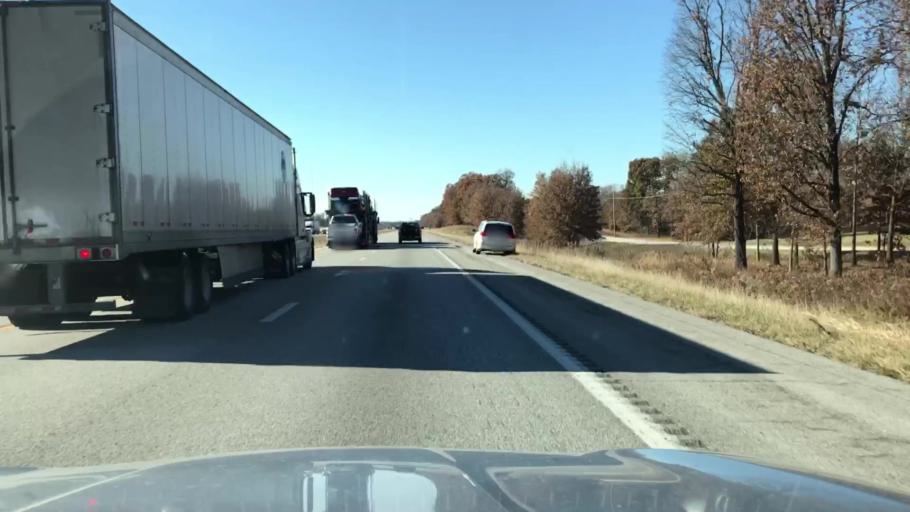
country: US
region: Missouri
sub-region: Jasper County
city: Duenweg
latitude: 37.0822
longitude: -94.3440
